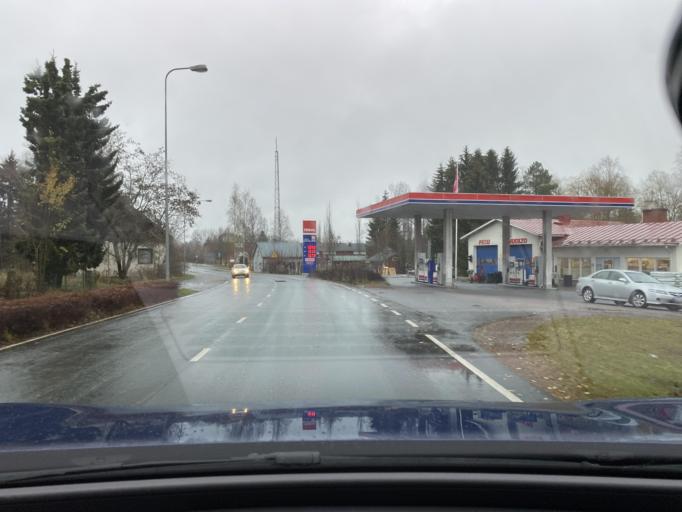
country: FI
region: Varsinais-Suomi
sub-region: Loimaa
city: Alastaro
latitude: 60.9488
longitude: 22.8650
